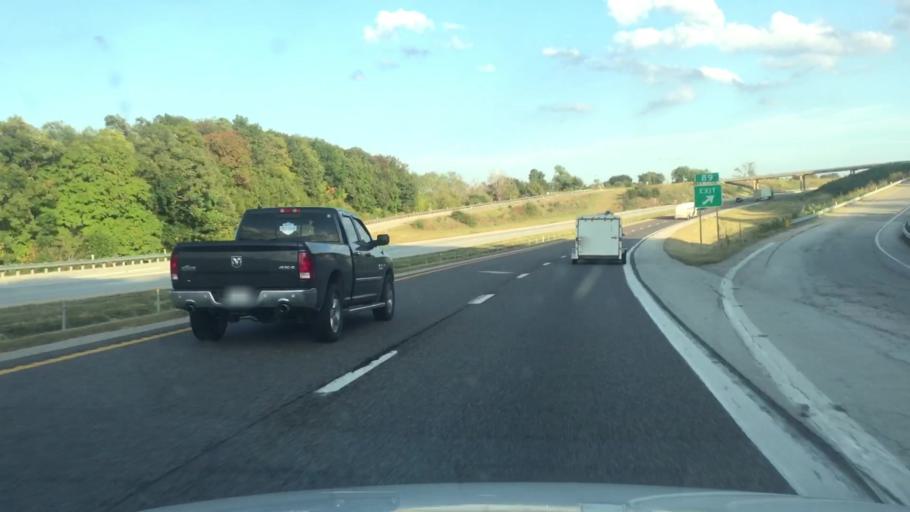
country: US
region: Missouri
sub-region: Cooper County
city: Boonville
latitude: 38.9466
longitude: -92.9953
